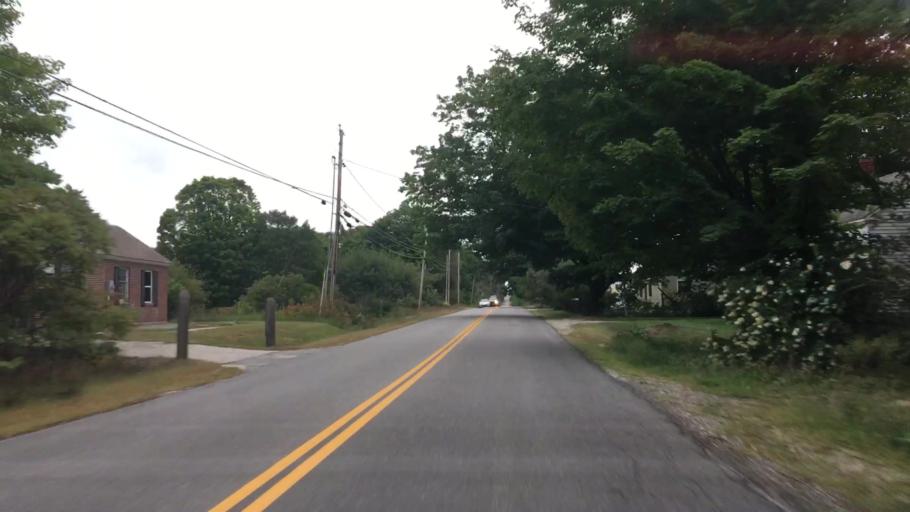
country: US
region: Maine
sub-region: Cumberland County
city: Yarmouth
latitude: 43.8957
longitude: -70.1916
